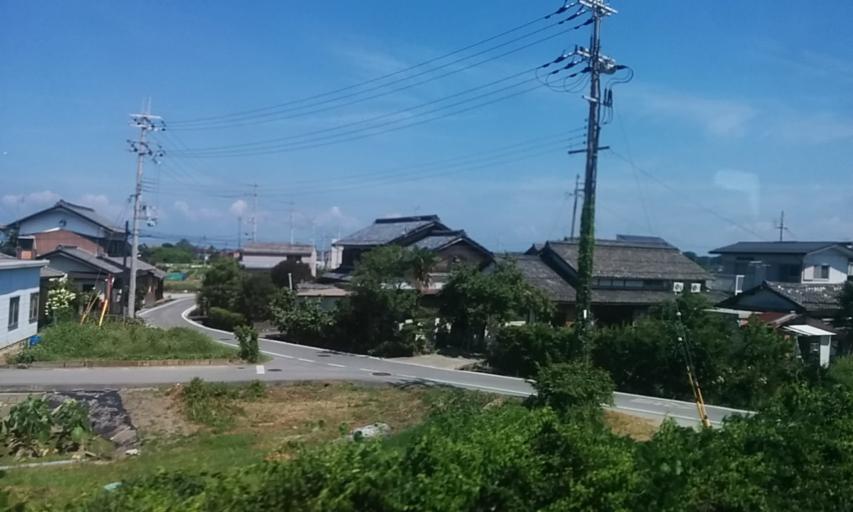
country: JP
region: Shiga Prefecture
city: Hikone
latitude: 35.2324
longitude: 136.2330
